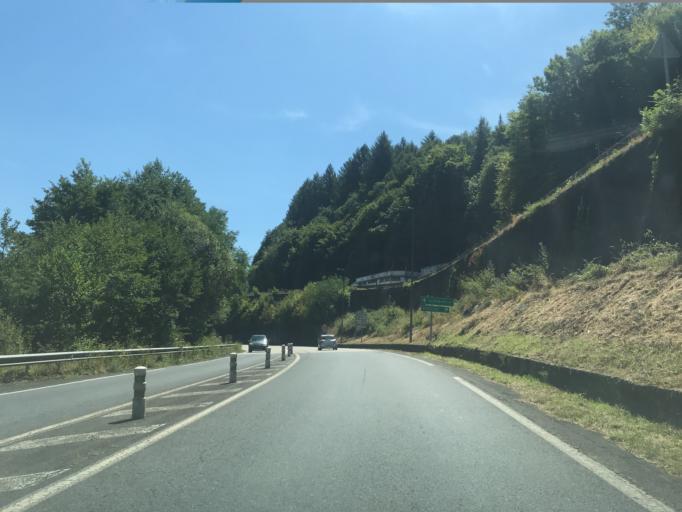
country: FR
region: Limousin
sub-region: Departement de la Correze
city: Laguenne
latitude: 45.2495
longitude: 1.7660
